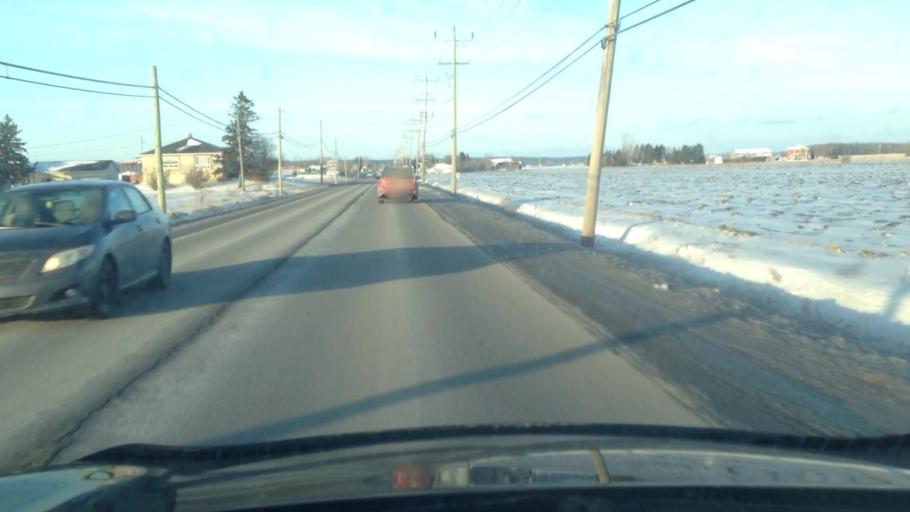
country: CA
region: Quebec
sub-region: Lanaudiere
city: Saint-Lin-Laurentides
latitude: 45.8729
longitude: -73.7573
